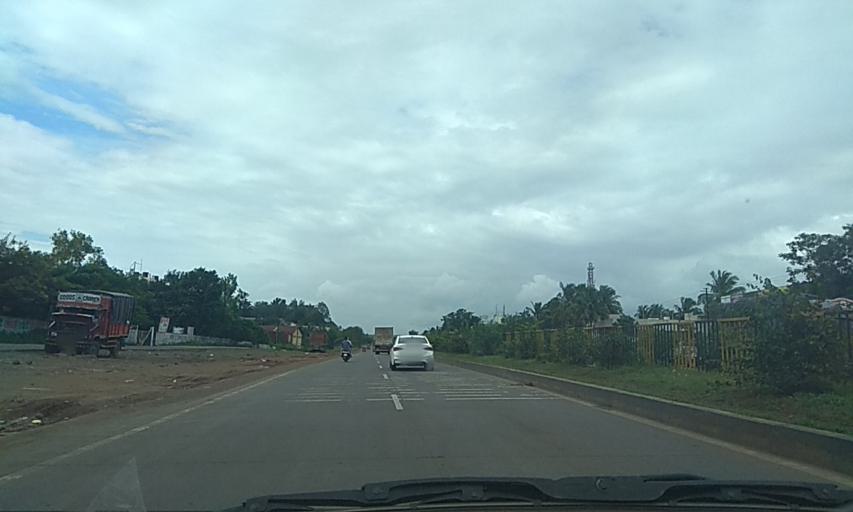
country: IN
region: Maharashtra
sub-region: Kolhapur
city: Kagal
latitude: 16.5845
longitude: 74.3097
